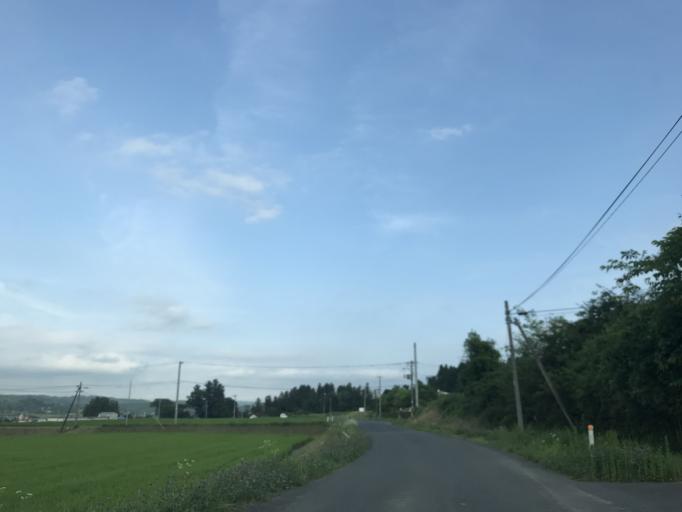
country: JP
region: Iwate
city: Ichinoseki
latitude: 38.8392
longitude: 141.1667
